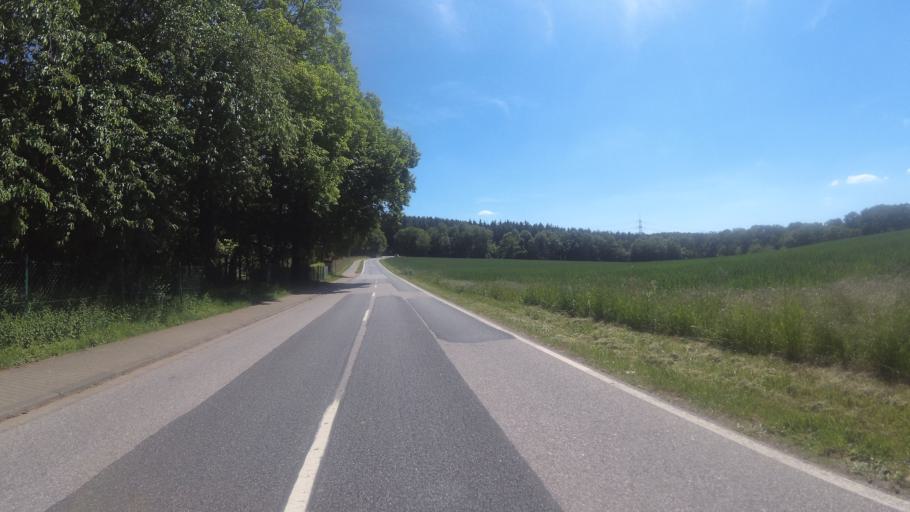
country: DE
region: Saarland
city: Eppelborn
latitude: 49.3796
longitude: 6.9521
